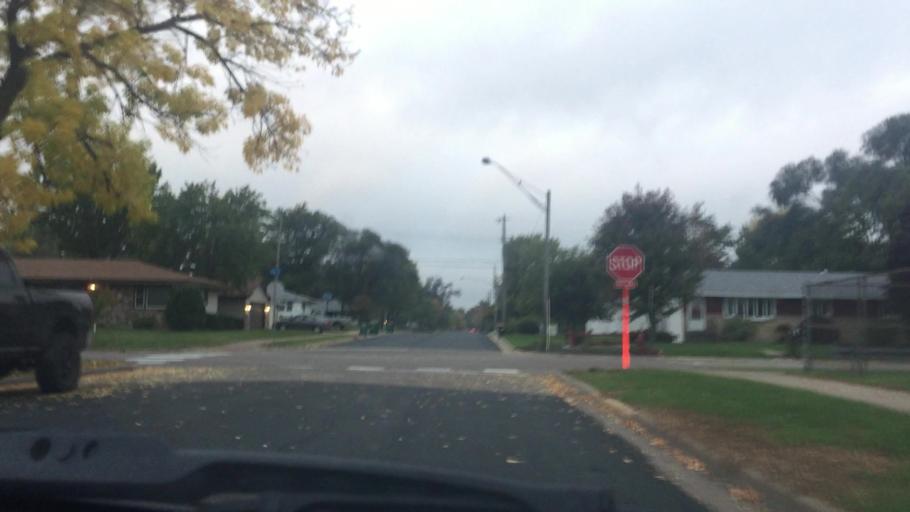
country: US
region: Minnesota
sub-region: Anoka County
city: Spring Lake Park
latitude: 45.1115
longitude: -93.2480
